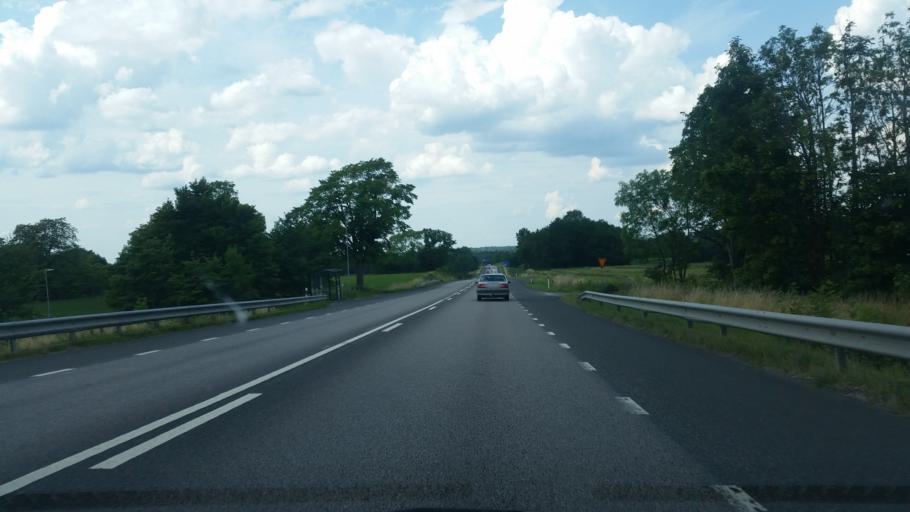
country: SE
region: Vaestra Goetaland
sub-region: Skara Kommun
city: Axvall
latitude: 58.3852
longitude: 13.6627
